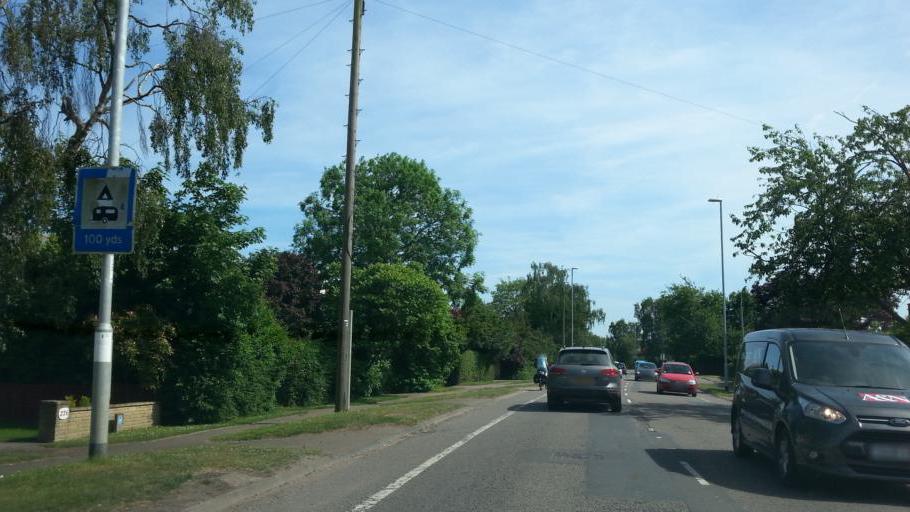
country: GB
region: England
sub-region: Cambridgeshire
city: Grantchester
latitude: 52.1649
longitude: 0.1209
